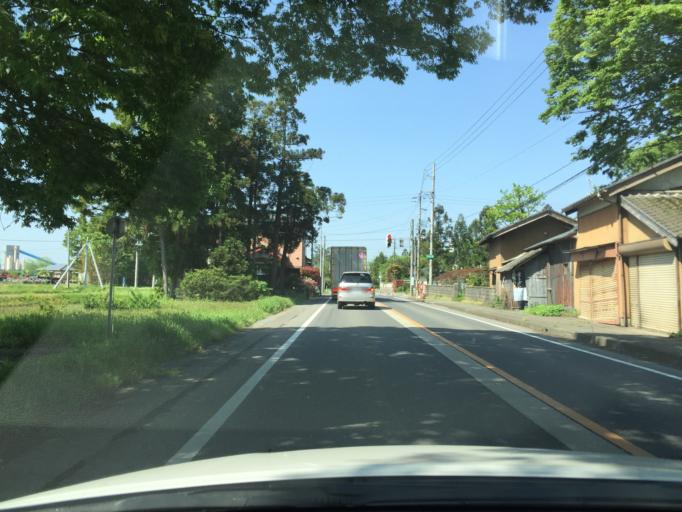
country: JP
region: Niigata
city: Muramatsu
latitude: 37.7146
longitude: 139.2145
